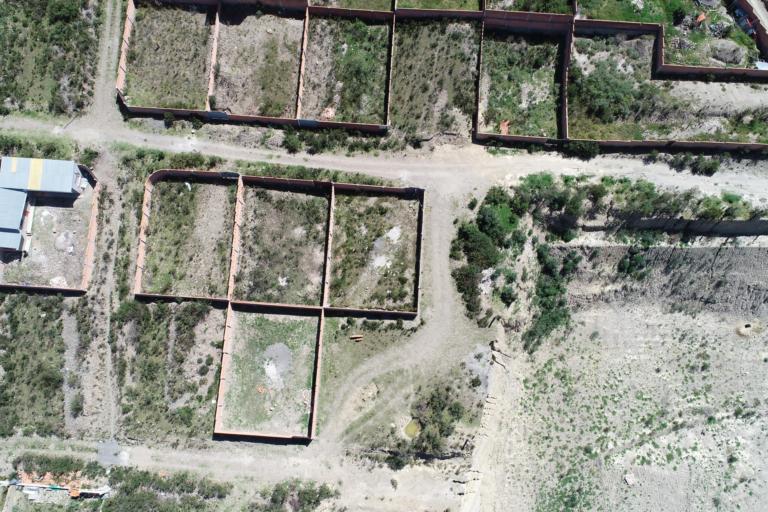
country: BO
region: La Paz
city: La Paz
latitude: -16.5043
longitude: -68.0576
